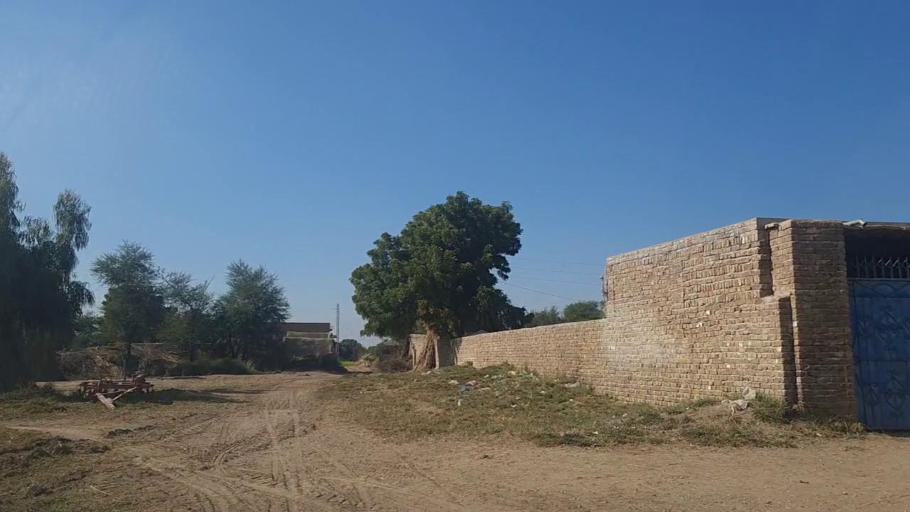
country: PK
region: Sindh
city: Sinjhoro
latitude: 26.1541
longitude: 68.8580
